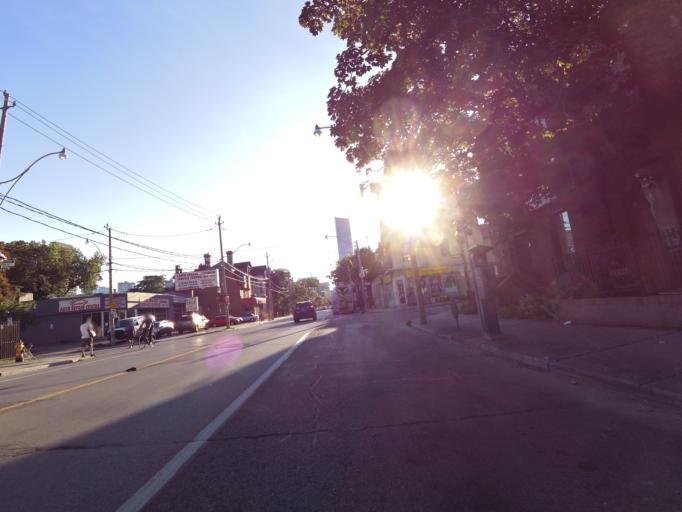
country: CA
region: Ontario
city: Toronto
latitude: 43.6616
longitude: -79.3704
